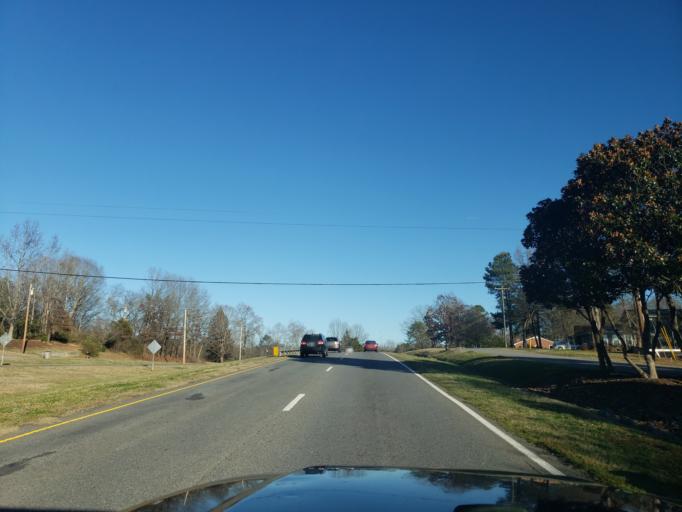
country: US
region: North Carolina
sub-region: Gaston County
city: Bessemer City
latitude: 35.2576
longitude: -81.2530
